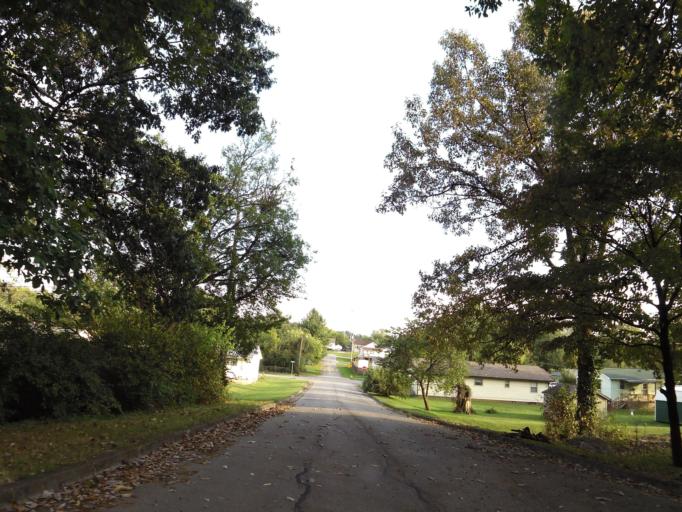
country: US
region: Tennessee
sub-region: Blount County
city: Alcoa
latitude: 35.7765
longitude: -83.9622
